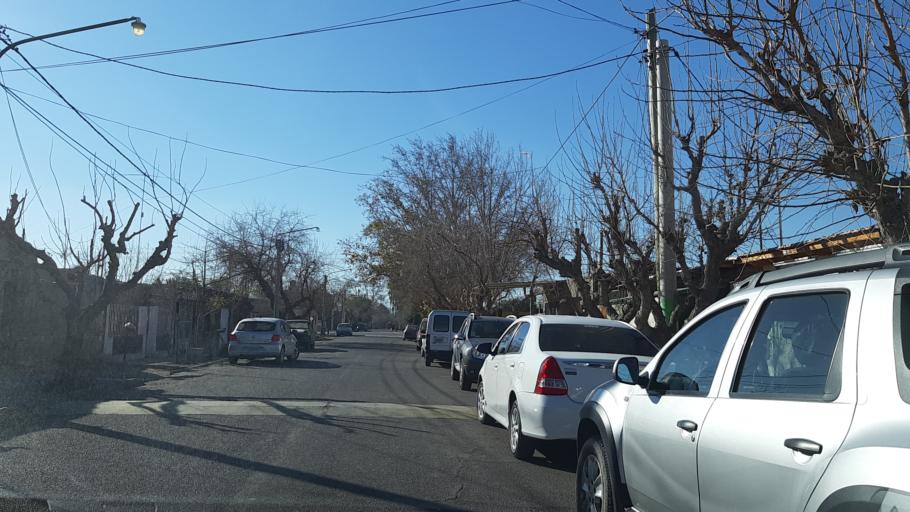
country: AR
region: San Juan
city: San Juan
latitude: -31.5378
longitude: -68.5722
